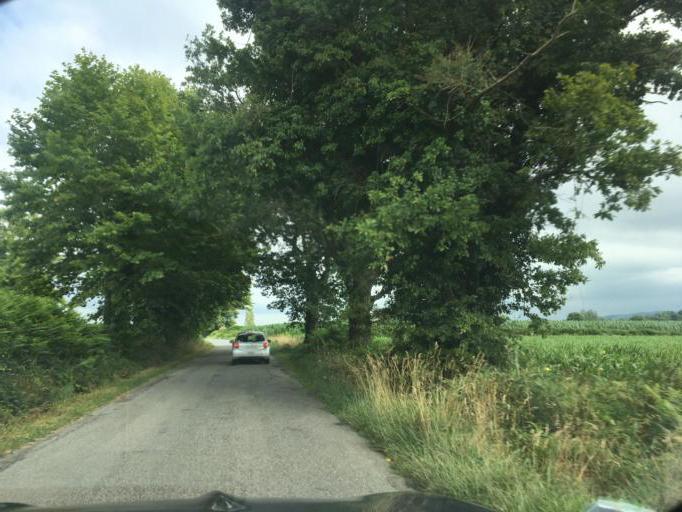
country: FR
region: Aquitaine
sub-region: Departement des Pyrenees-Atlantiques
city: Buros
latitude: 43.3148
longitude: -0.2909
